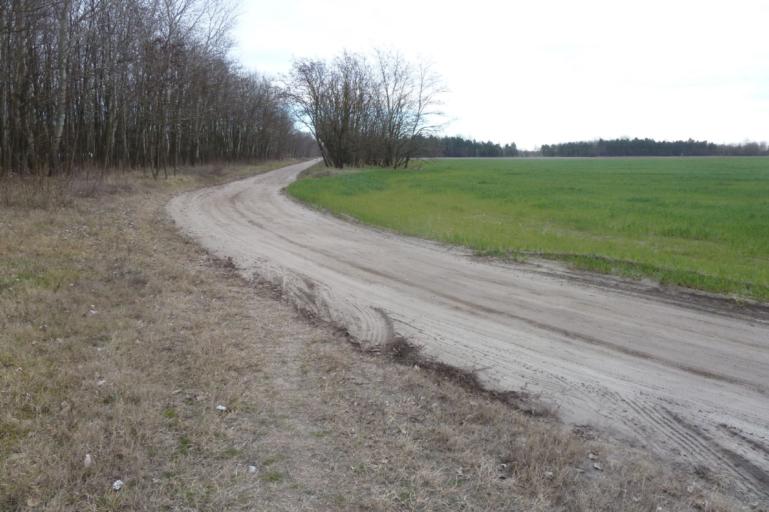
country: HU
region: Bacs-Kiskun
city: Jaszszentlaszlo
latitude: 46.5911
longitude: 19.7822
